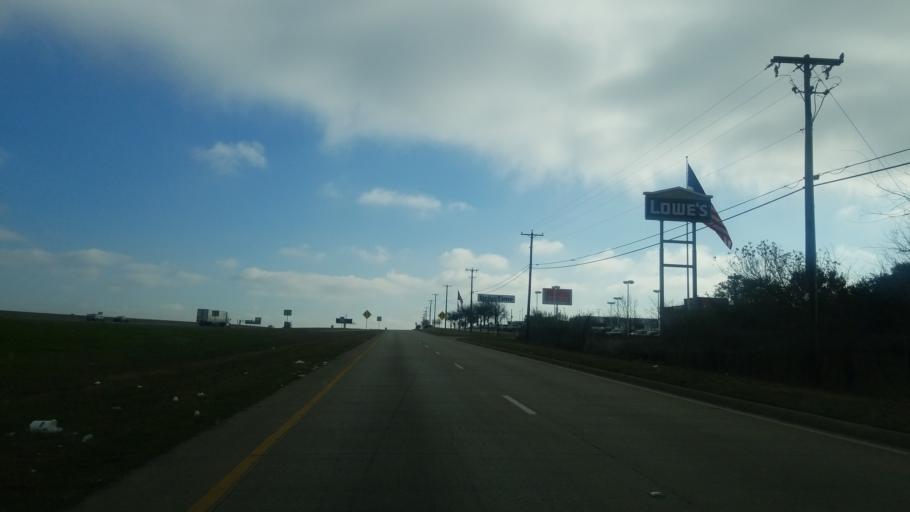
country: US
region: Texas
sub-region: Dallas County
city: Duncanville
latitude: 32.6446
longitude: -96.8550
